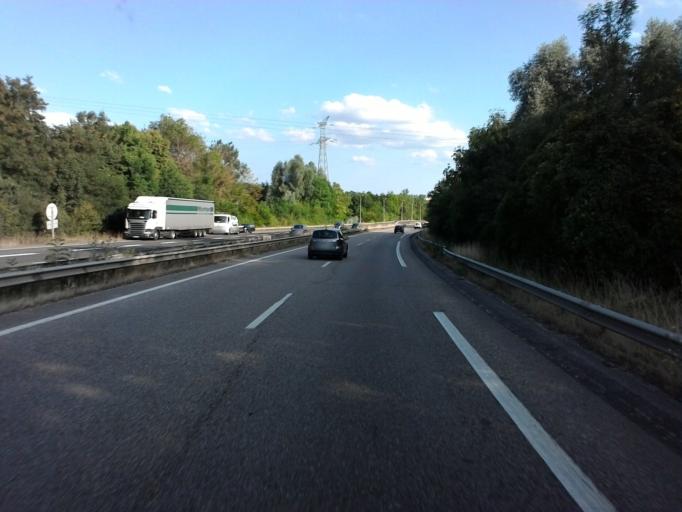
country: FR
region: Lorraine
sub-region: Departement de Meurthe-et-Moselle
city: Richardmenil
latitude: 48.5867
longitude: 6.1763
